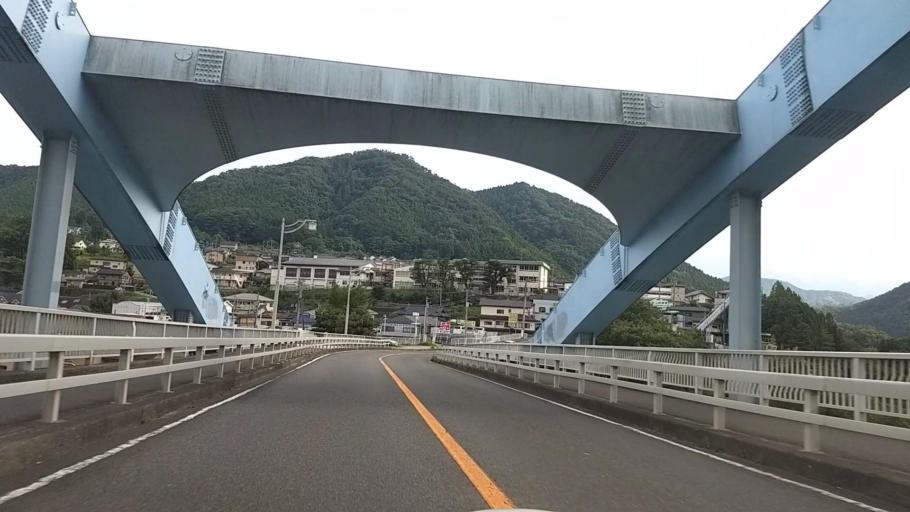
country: JP
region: Yamanashi
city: Uenohara
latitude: 35.6129
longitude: 139.1562
